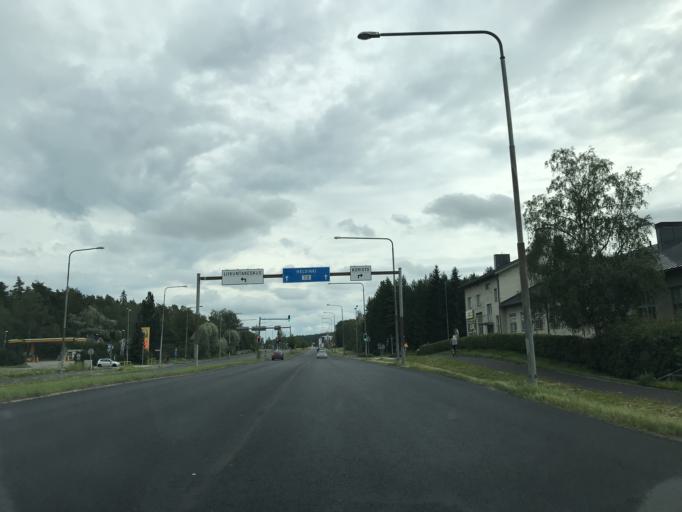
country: FI
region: Varsinais-Suomi
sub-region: Turku
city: Kaarina
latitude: 60.4116
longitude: 22.3511
